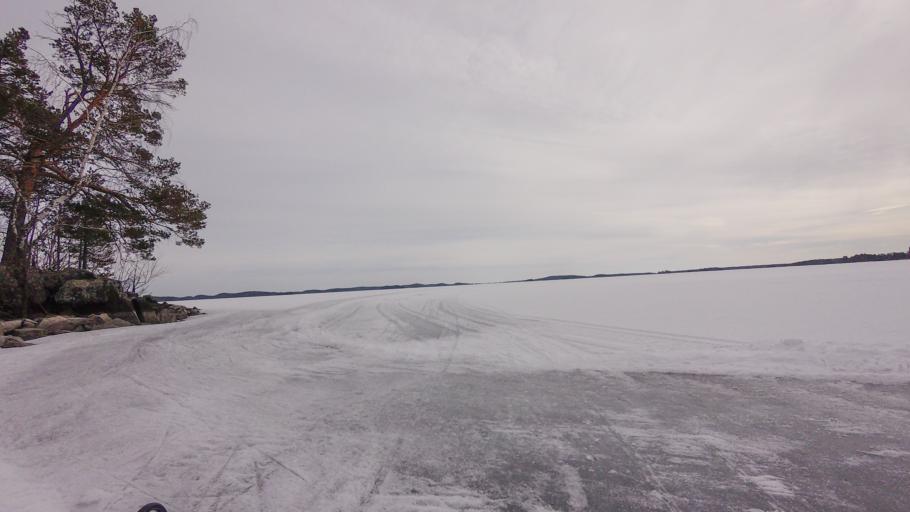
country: FI
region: Southern Savonia
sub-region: Savonlinna
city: Rantasalmi
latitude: 62.1133
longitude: 28.3766
